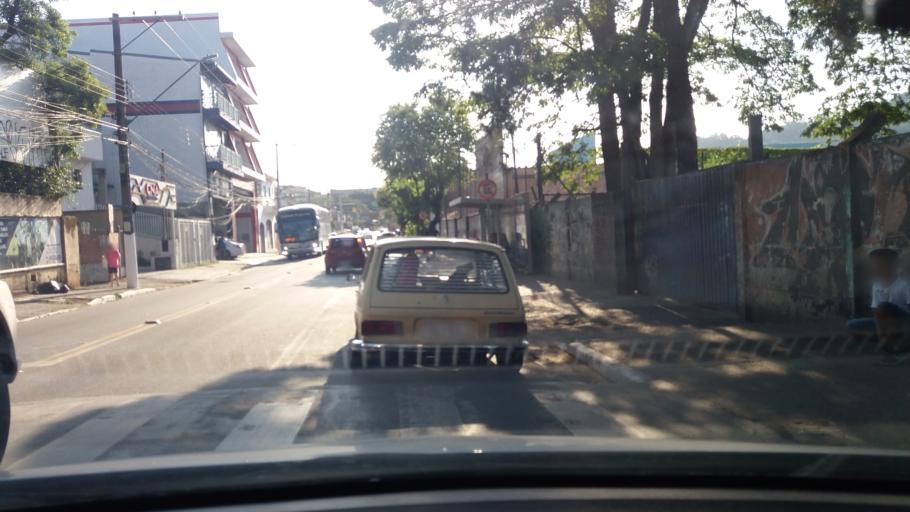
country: BR
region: Sao Paulo
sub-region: Mairipora
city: Mairipora
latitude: -23.3188
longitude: -46.5888
